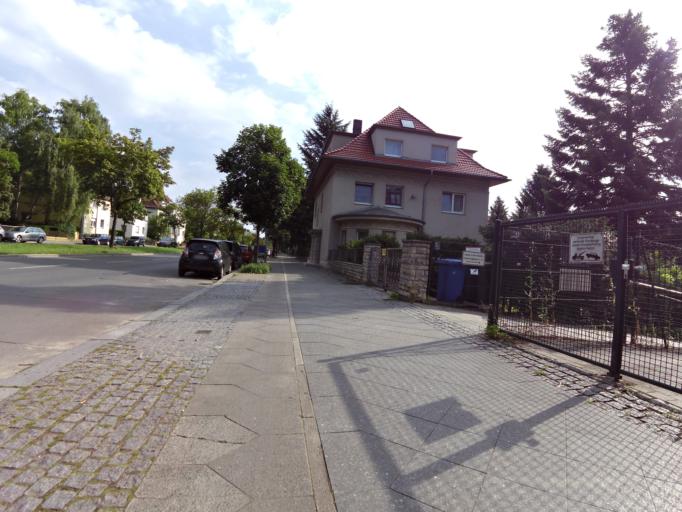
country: DE
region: Berlin
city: Lichterfelde
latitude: 52.4323
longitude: 13.3109
